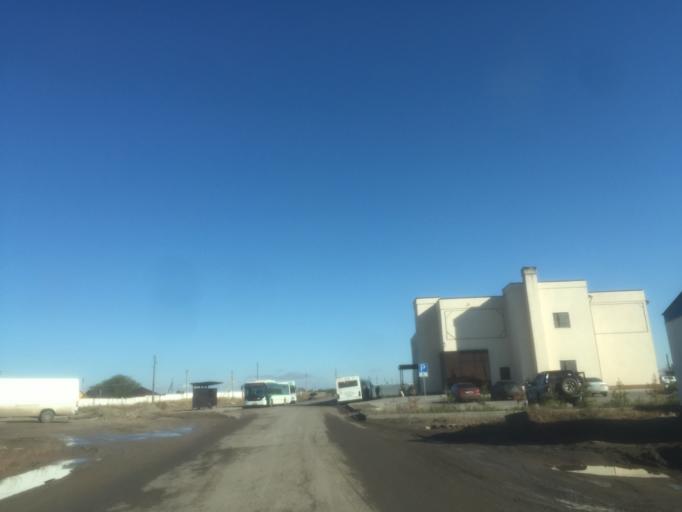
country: KZ
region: Astana Qalasy
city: Astana
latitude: 51.2125
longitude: 71.3545
